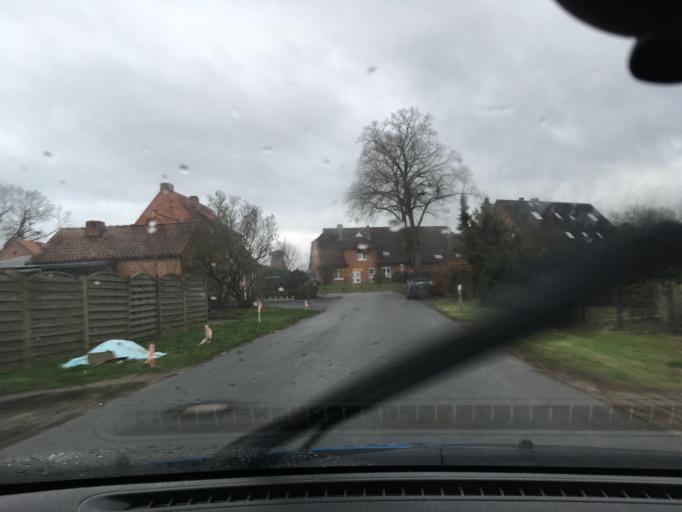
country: DE
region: Lower Saxony
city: Hittbergen
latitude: 53.3453
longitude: 10.5928
